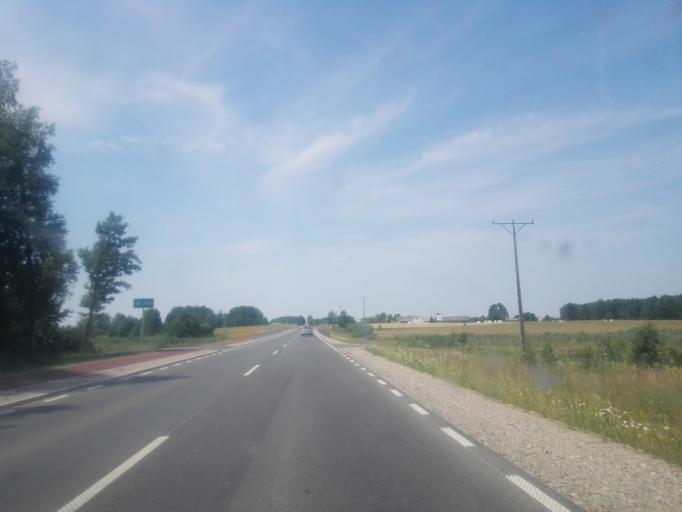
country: PL
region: Podlasie
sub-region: Powiat sejnenski
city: Krasnopol
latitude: 54.1084
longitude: 23.2665
